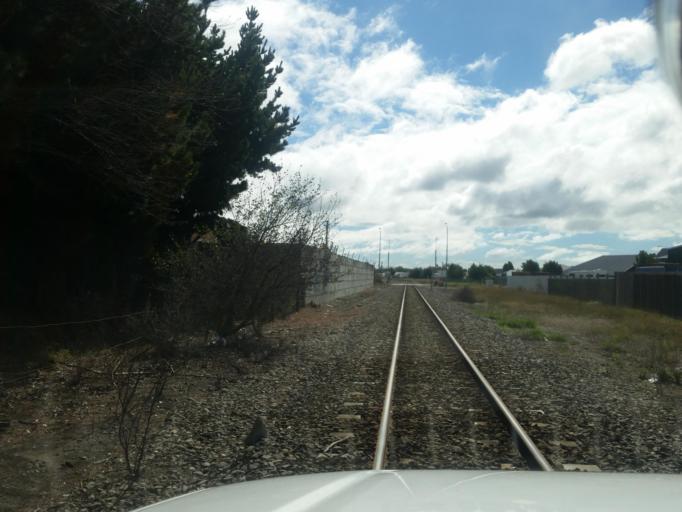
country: NZ
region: Canterbury
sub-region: Waimakariri District
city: Kaiapoi
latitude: -43.3932
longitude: 172.6567
